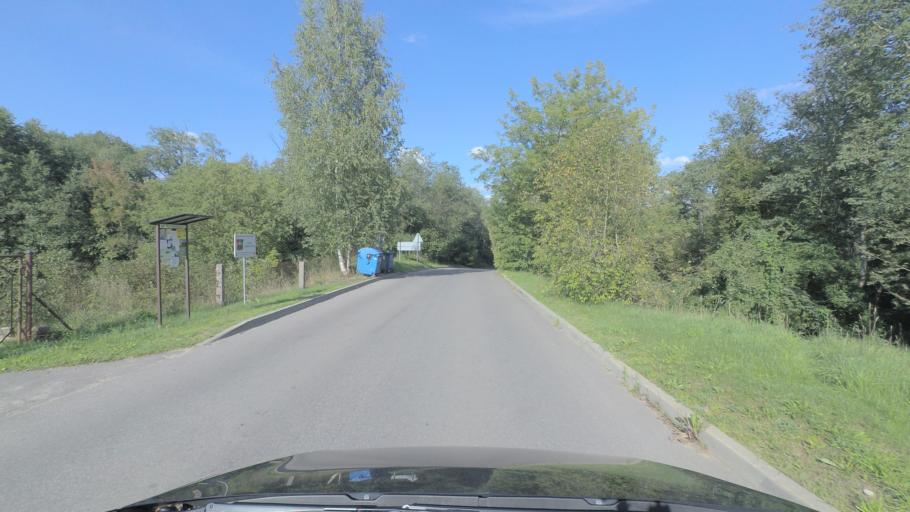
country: LT
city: Nemencine
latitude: 54.8585
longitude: 25.3866
